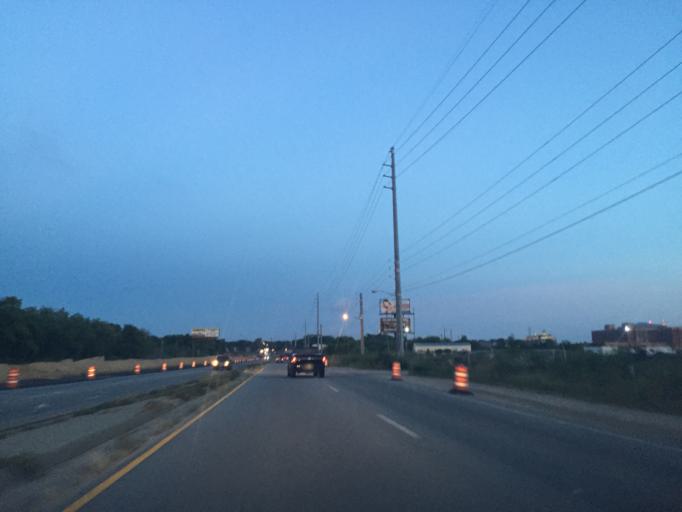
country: US
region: Georgia
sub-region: Chatham County
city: Savannah
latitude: 32.0739
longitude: -81.0761
